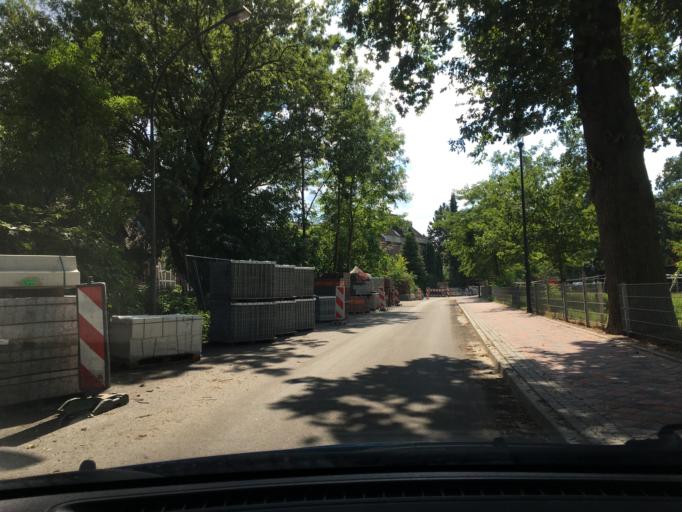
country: DE
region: Lower Saxony
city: Harmstorf
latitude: 53.3923
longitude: 10.0402
